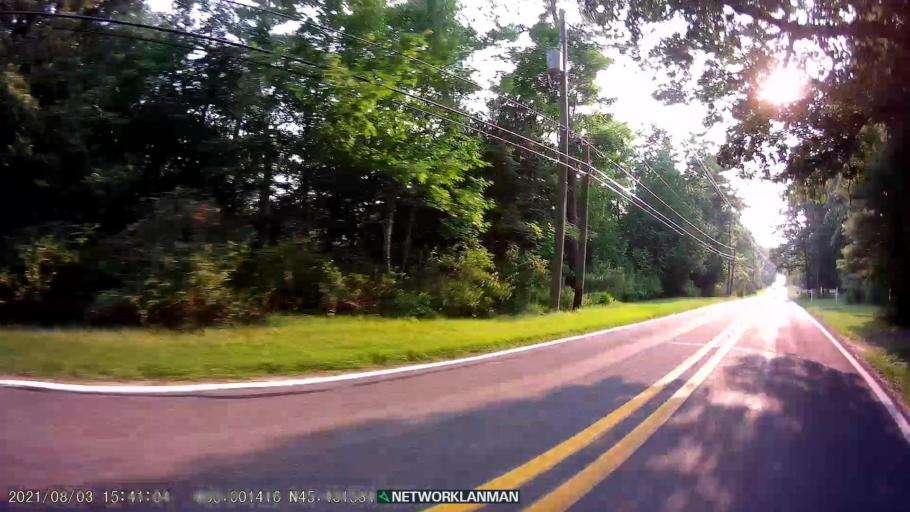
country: US
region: Michigan
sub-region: Emmet County
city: Harbor Springs
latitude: 45.4315
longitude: -85.0024
